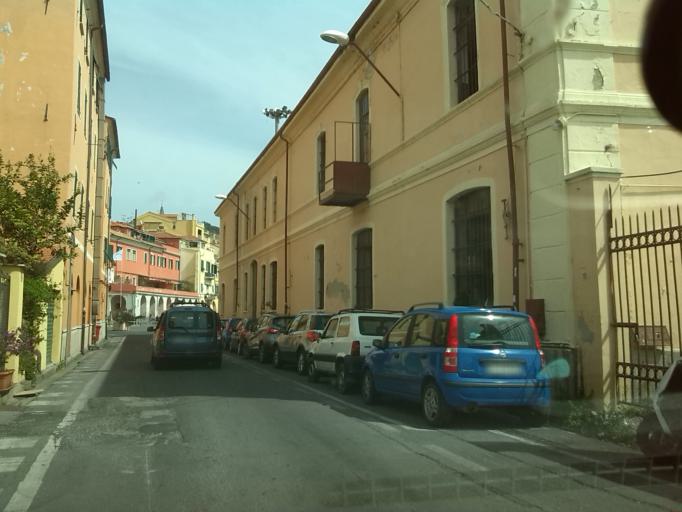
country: IT
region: Liguria
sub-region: Provincia di Imperia
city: Imperia
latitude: 43.8871
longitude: 8.0395
